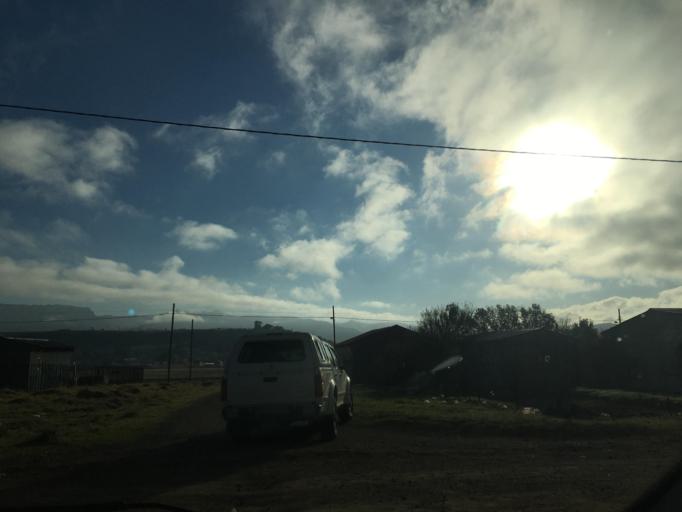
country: ZA
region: Eastern Cape
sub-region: Chris Hani District Municipality
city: Elliot
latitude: -31.3354
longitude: 27.8398
